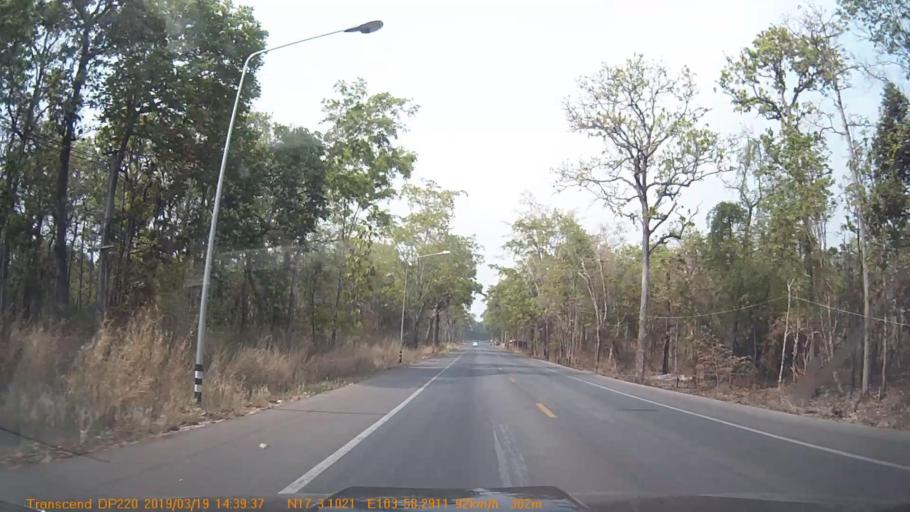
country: TH
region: Sakon Nakhon
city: Phu Phan
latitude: 17.0522
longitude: 103.9715
